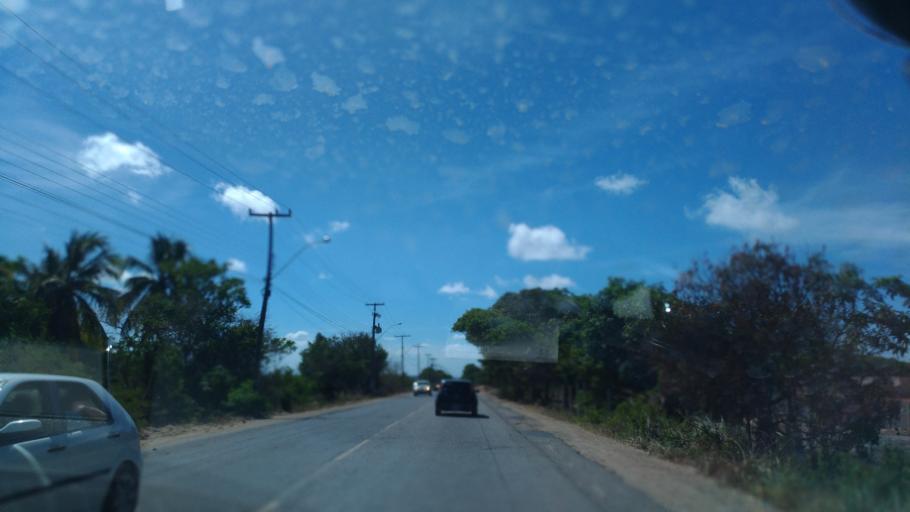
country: BR
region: Alagoas
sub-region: Marechal Deodoro
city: Marechal Deodoro
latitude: -9.7655
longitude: -35.8546
